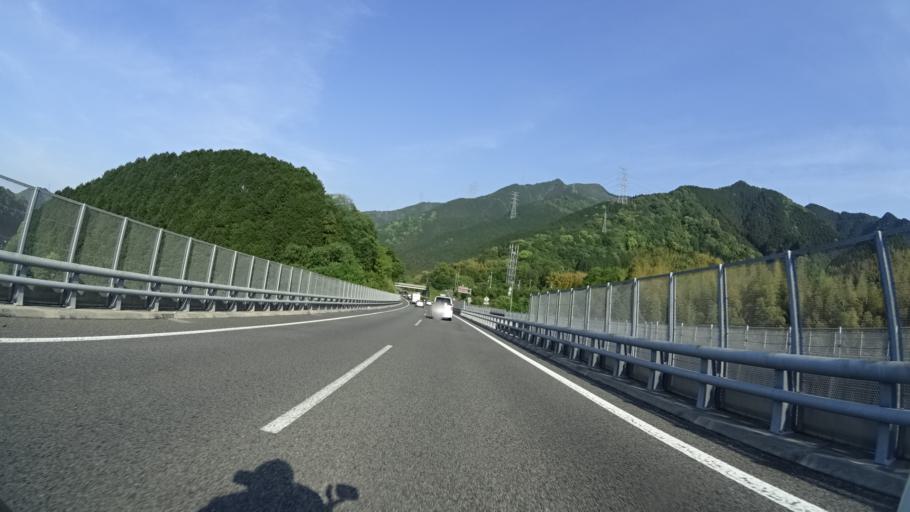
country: JP
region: Ehime
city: Saijo
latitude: 33.8850
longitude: 133.1814
